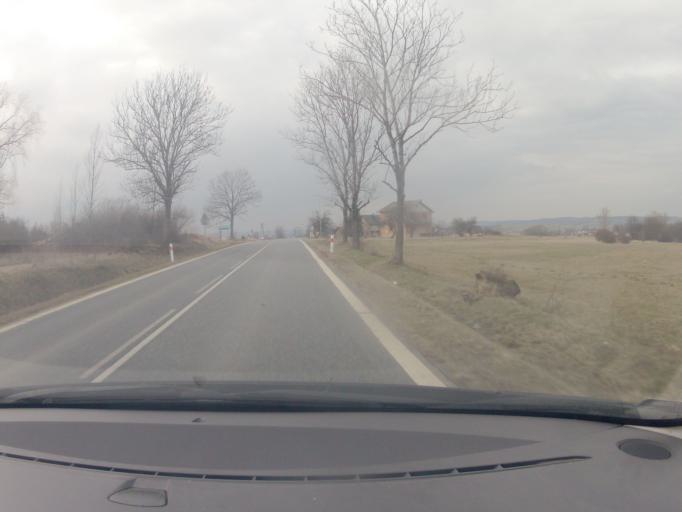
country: PL
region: Subcarpathian Voivodeship
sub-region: Powiat jasielski
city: Nowy Zmigrod
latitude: 49.5861
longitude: 21.5466
